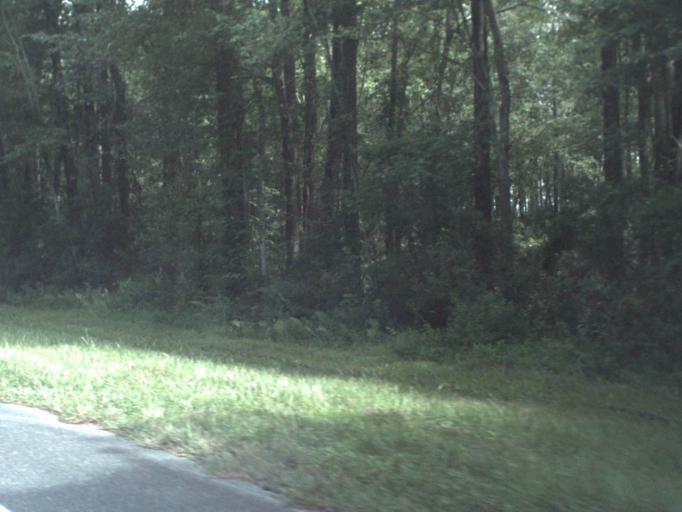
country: US
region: Florida
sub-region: Columbia County
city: Watertown
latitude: 30.1509
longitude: -82.5530
